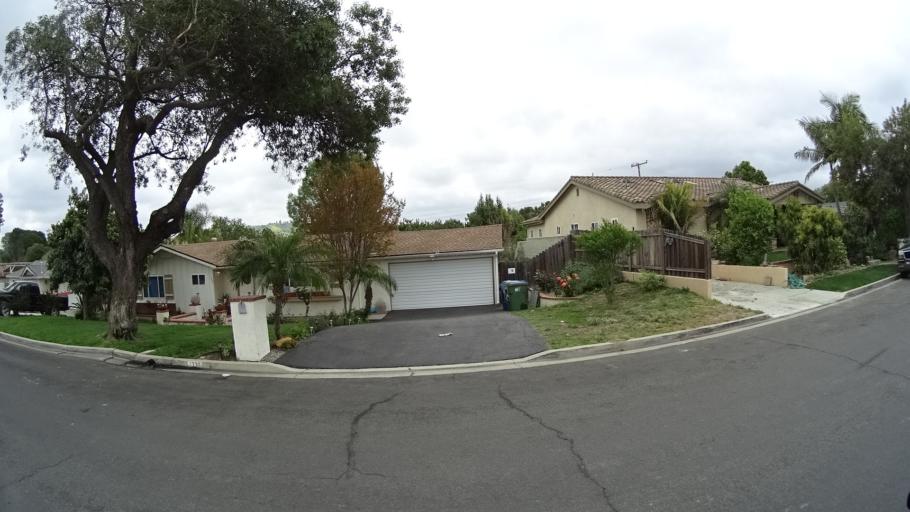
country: US
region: California
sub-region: Ventura County
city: Thousand Oaks
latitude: 34.2115
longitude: -118.8564
